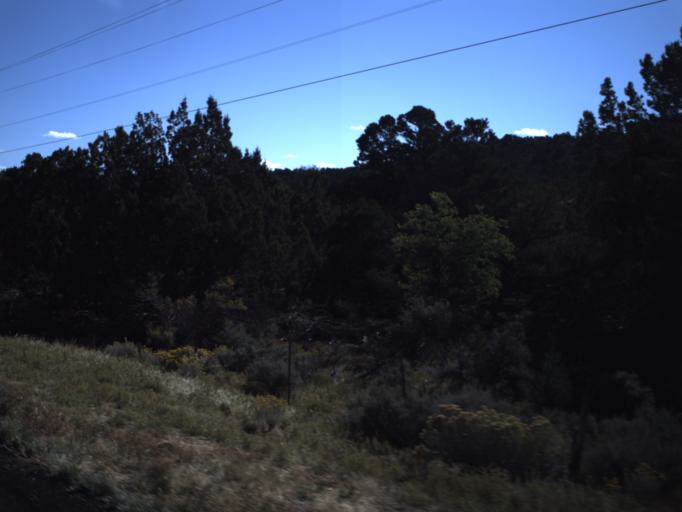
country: US
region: Utah
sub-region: Iron County
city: Cedar City
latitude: 37.6199
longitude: -113.3281
